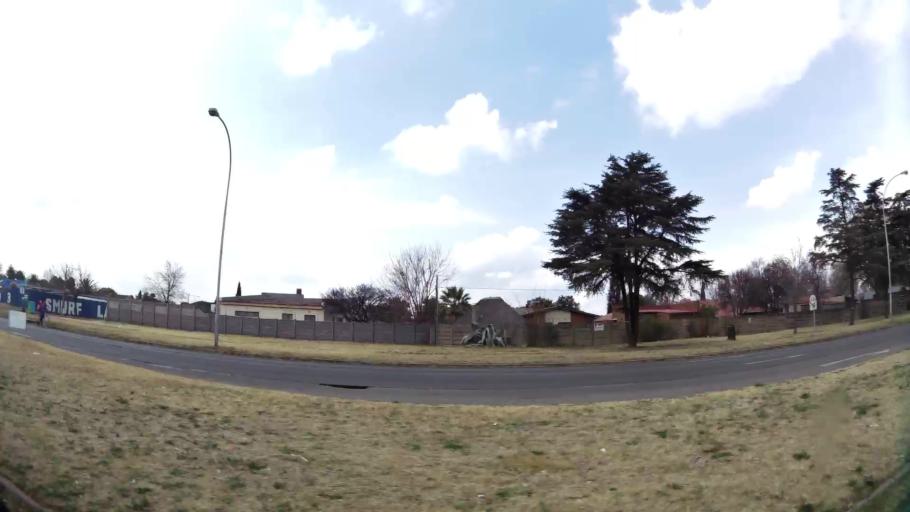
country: ZA
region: Gauteng
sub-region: Sedibeng District Municipality
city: Vanderbijlpark
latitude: -26.7093
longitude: 27.8360
